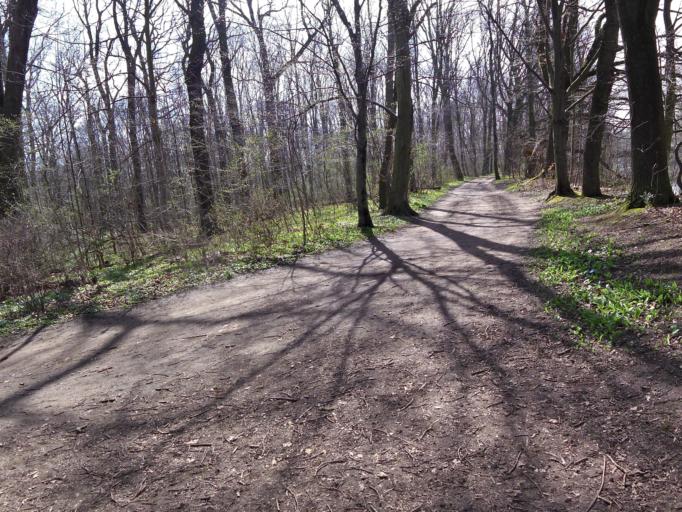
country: DE
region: Saxony
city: Leipzig
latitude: 51.3606
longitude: 12.3423
